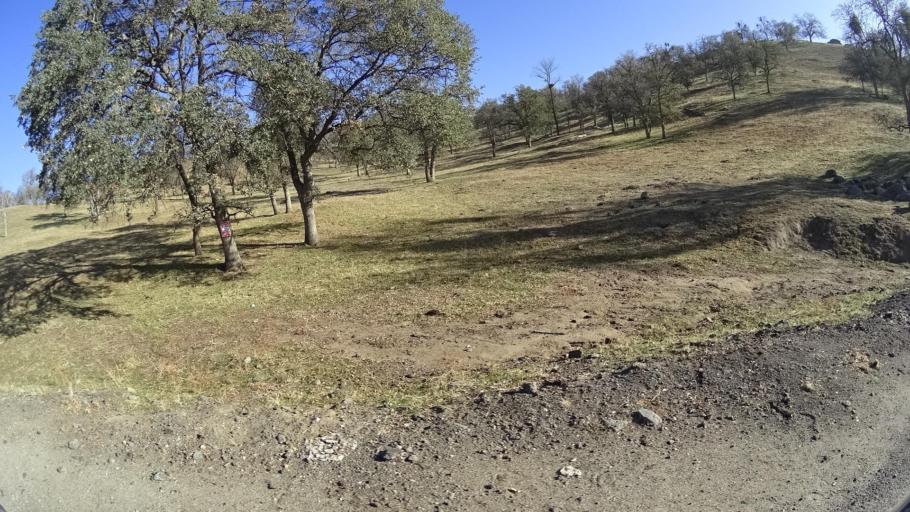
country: US
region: California
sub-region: Kern County
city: Alta Sierra
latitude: 35.7320
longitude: -118.8137
